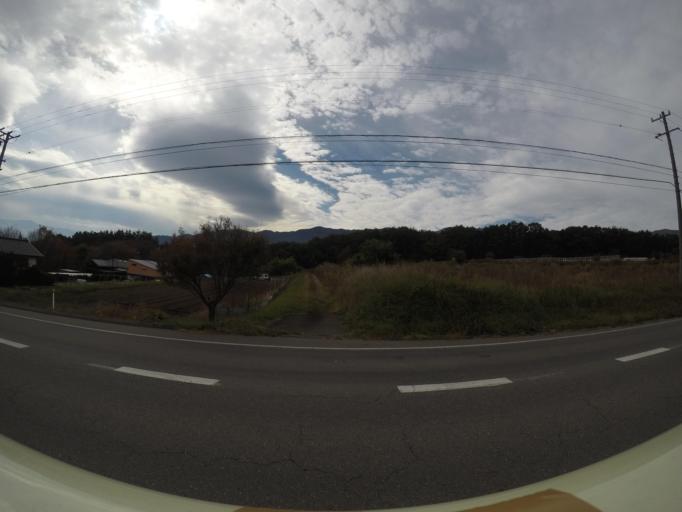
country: JP
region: Nagano
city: Ina
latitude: 35.8601
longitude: 137.9031
